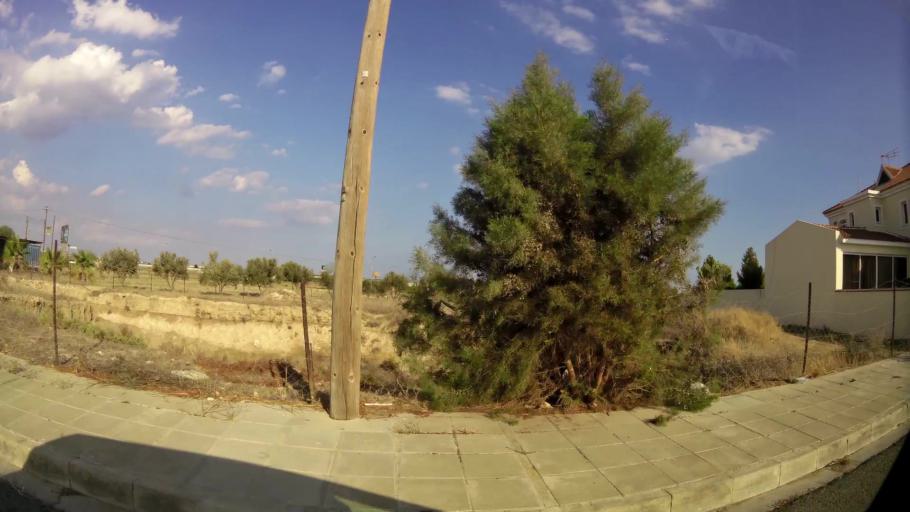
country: CY
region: Larnaka
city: Dhromolaxia
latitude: 34.8762
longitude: 33.5977
